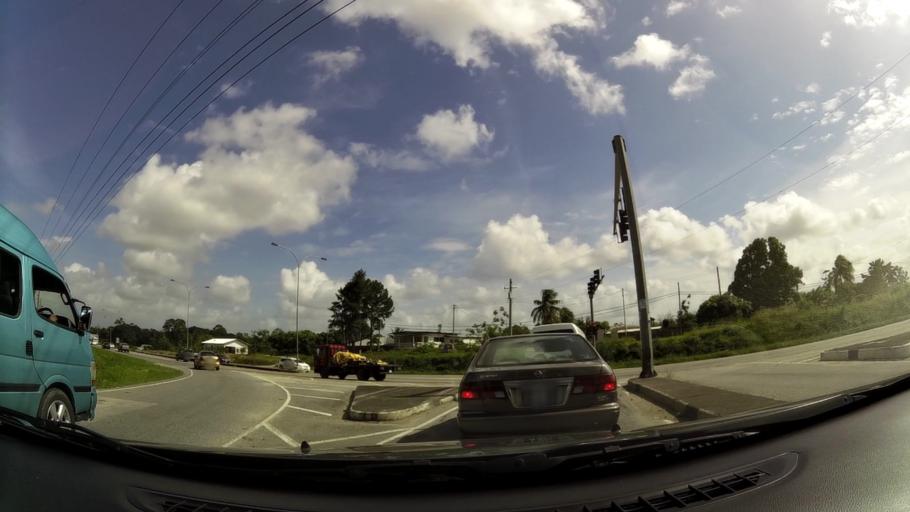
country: TT
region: Borough of Arima
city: Arima
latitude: 10.6203
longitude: -61.2538
